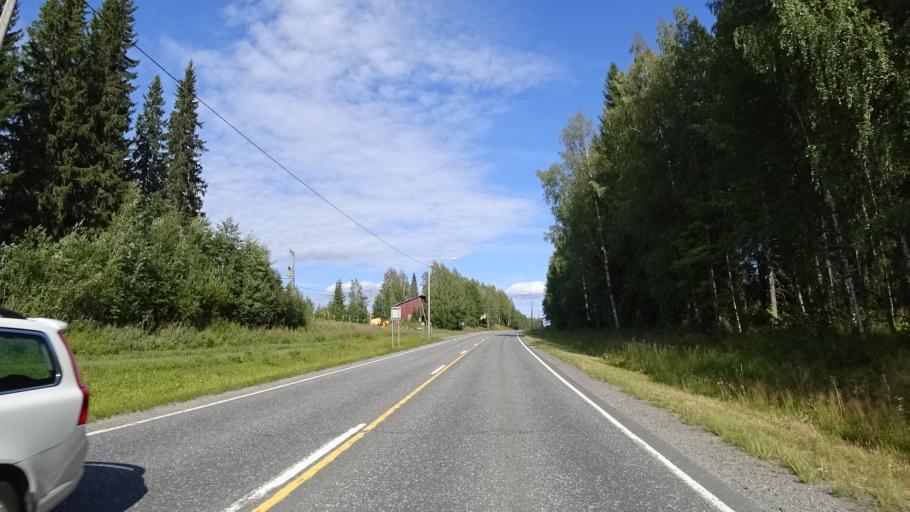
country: FI
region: North Karelia
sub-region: Joensuu
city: Eno
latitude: 62.8051
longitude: 30.1284
